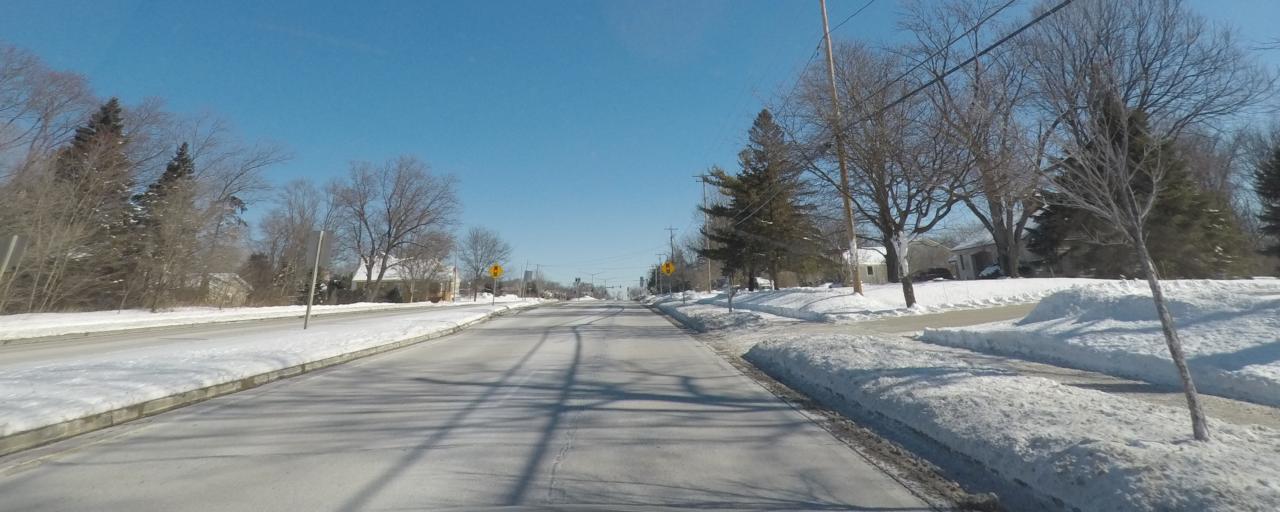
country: US
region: Wisconsin
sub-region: Waukesha County
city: New Berlin
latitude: 43.0169
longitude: -88.1306
